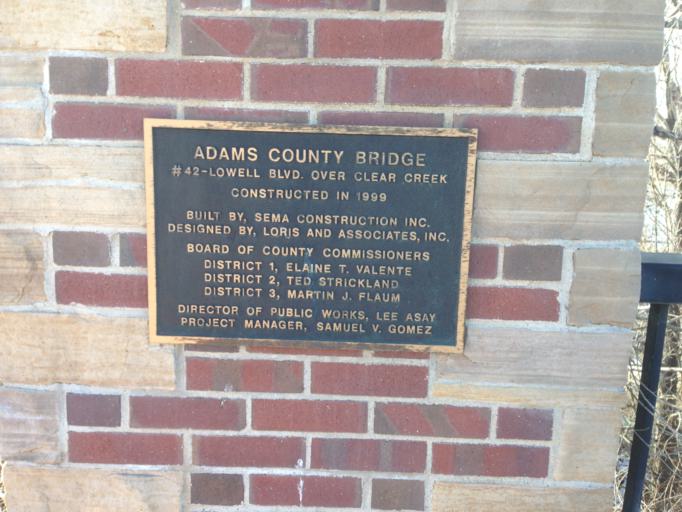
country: US
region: Colorado
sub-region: Adams County
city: Berkley
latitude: 39.7981
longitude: -105.0348
